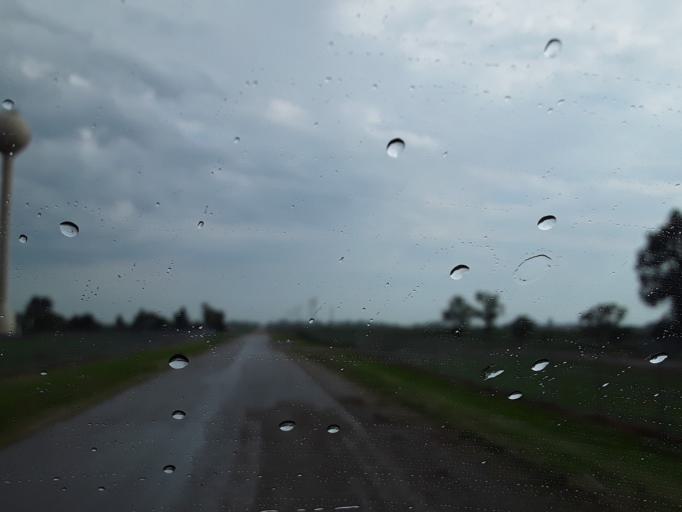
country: US
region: Nebraska
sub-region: Saunders County
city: Yutan
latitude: 41.1874
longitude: -96.4449
